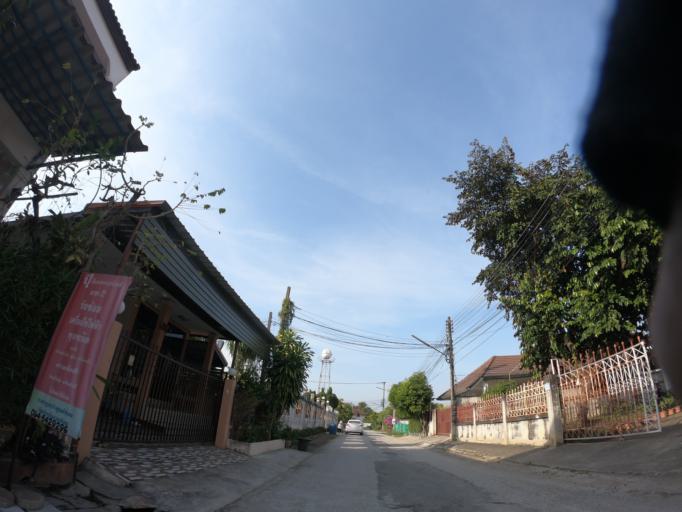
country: TH
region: Chiang Mai
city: Chiang Mai
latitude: 18.8292
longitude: 98.9894
